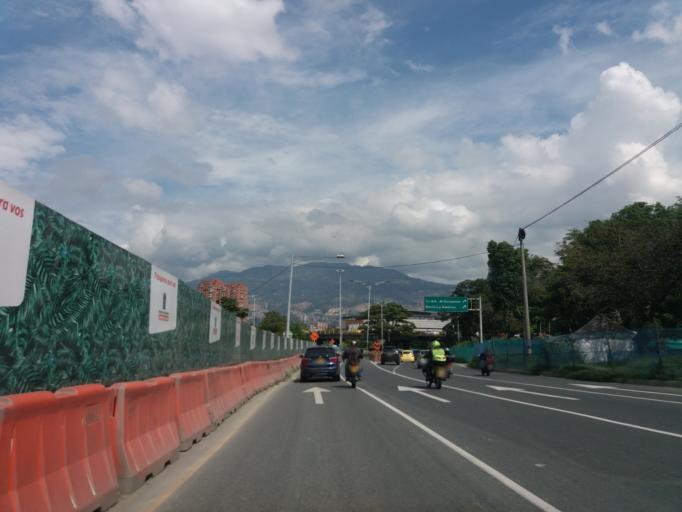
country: CO
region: Antioquia
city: Medellin
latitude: 6.2463
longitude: -75.5793
